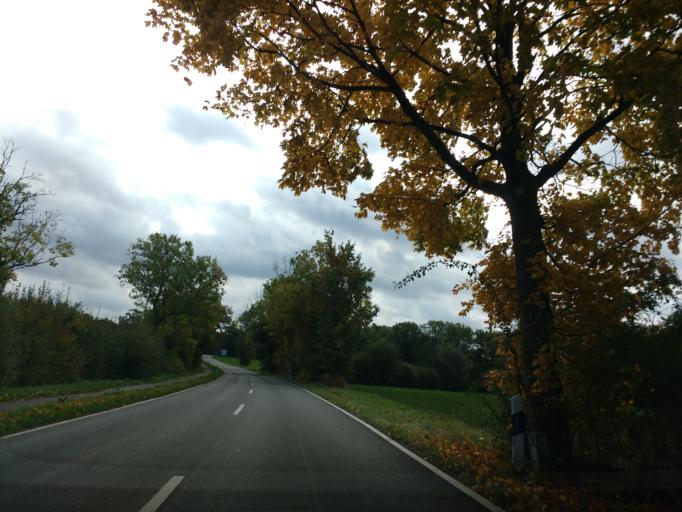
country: DE
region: Schleswig-Holstein
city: Travemuende
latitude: 53.9739
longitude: 10.8515
